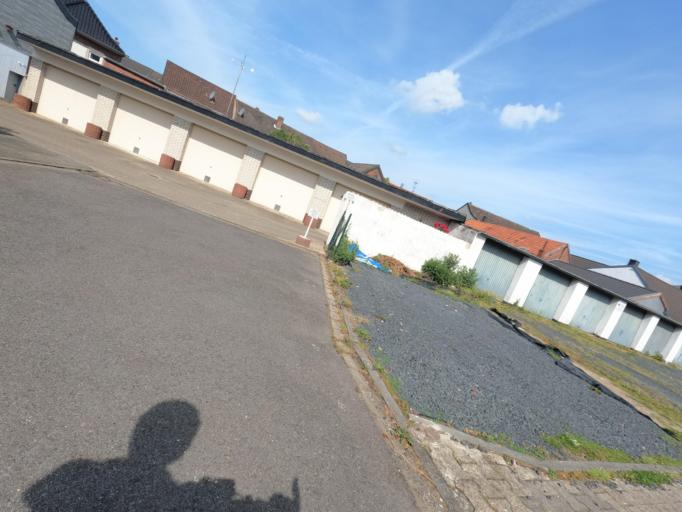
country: DE
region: North Rhine-Westphalia
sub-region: Regierungsbezirk Koln
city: Heinsberg
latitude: 51.0421
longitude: 6.1495
